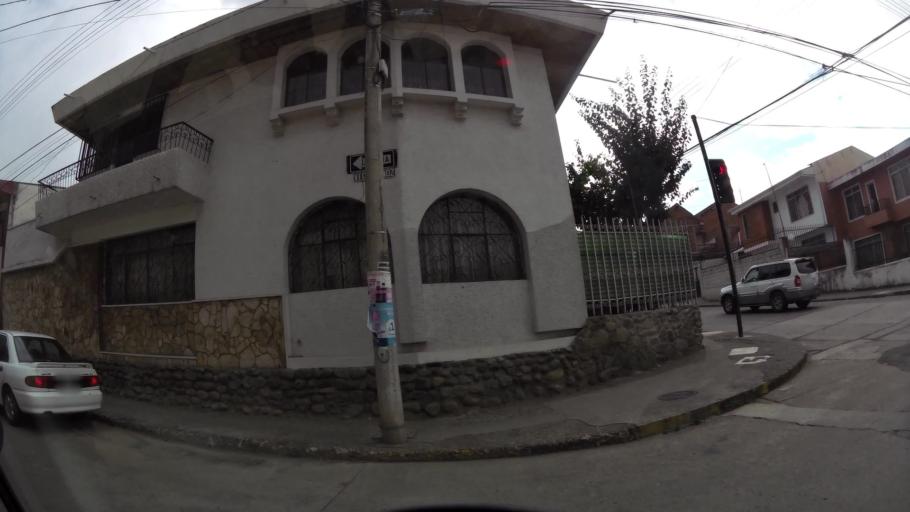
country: EC
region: Azuay
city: Cuenca
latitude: -2.8899
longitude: -79.0164
